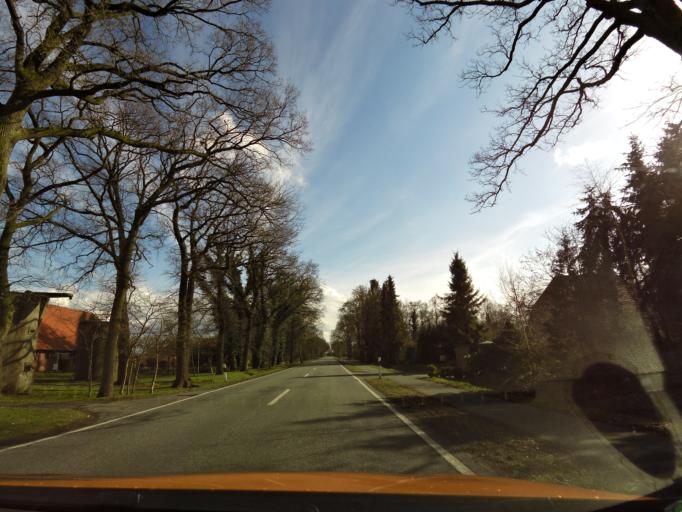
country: DE
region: Lower Saxony
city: Wardenburg
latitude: 53.0834
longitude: 8.2928
